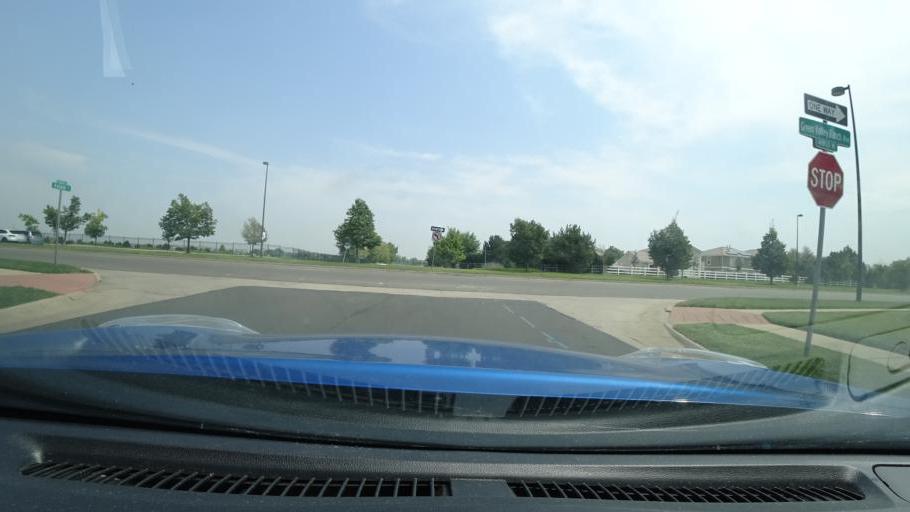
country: US
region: Colorado
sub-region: Adams County
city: Aurora
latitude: 39.7818
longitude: -104.7530
